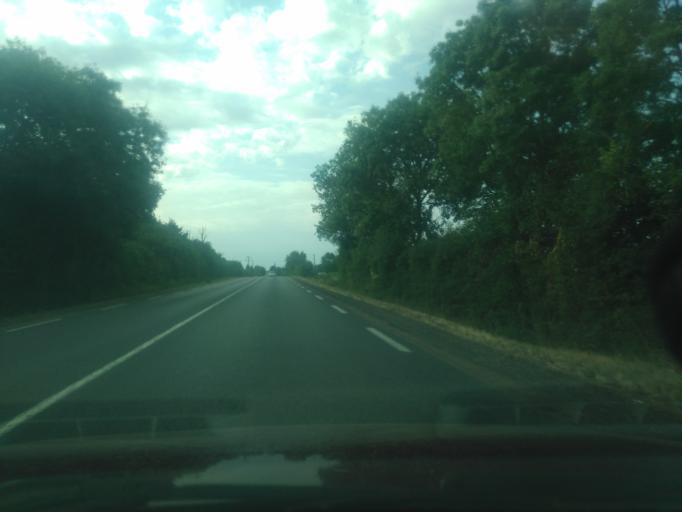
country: FR
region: Pays de la Loire
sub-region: Departement de la Vendee
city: Sainte-Cecile
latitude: 46.7493
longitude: -1.0935
